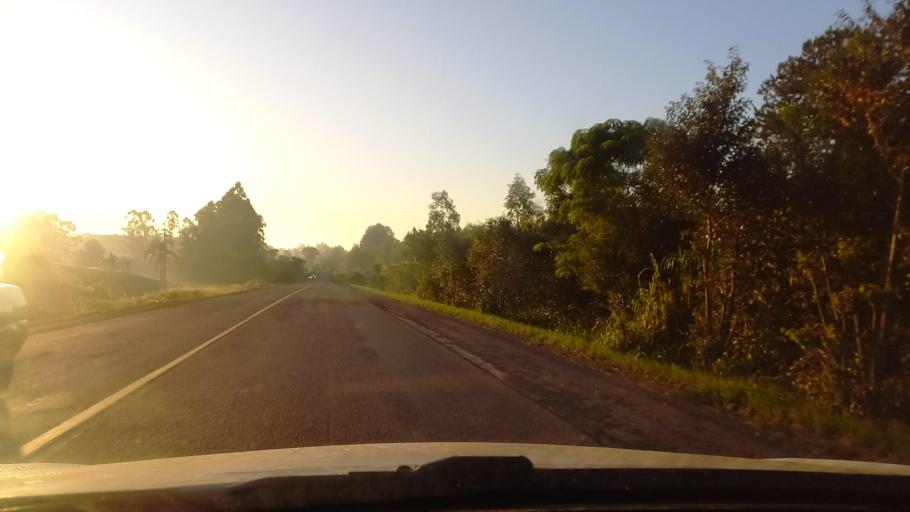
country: BR
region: Rio Grande do Sul
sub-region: Candelaria
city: Candelaria
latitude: -29.6807
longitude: -52.8273
